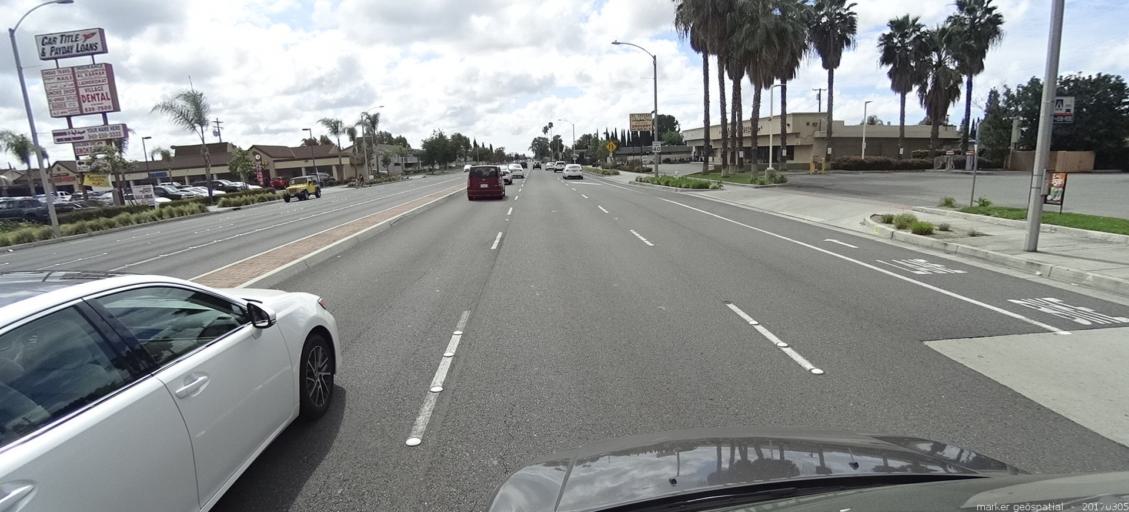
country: US
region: California
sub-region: Orange County
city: Stanton
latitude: 33.8175
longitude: -117.9590
